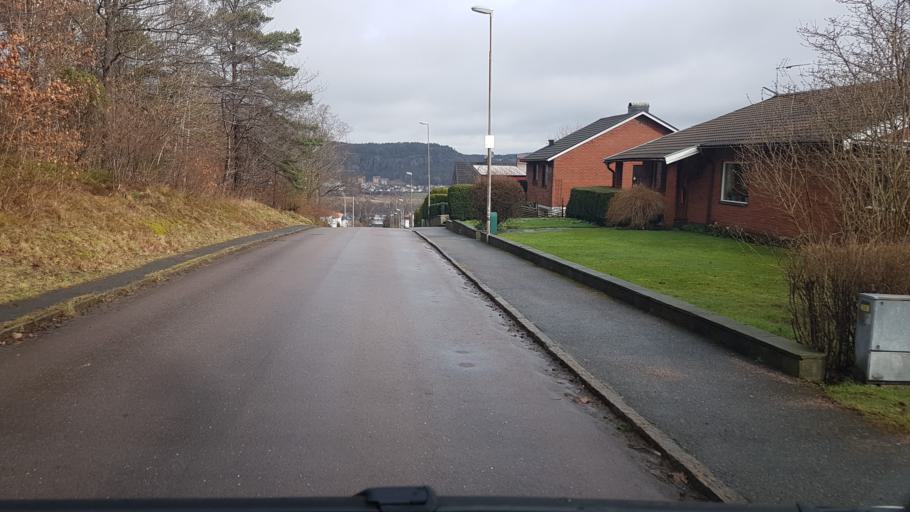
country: SE
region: Vaestra Goetaland
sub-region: Partille Kommun
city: Partille
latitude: 57.7253
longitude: 12.0658
